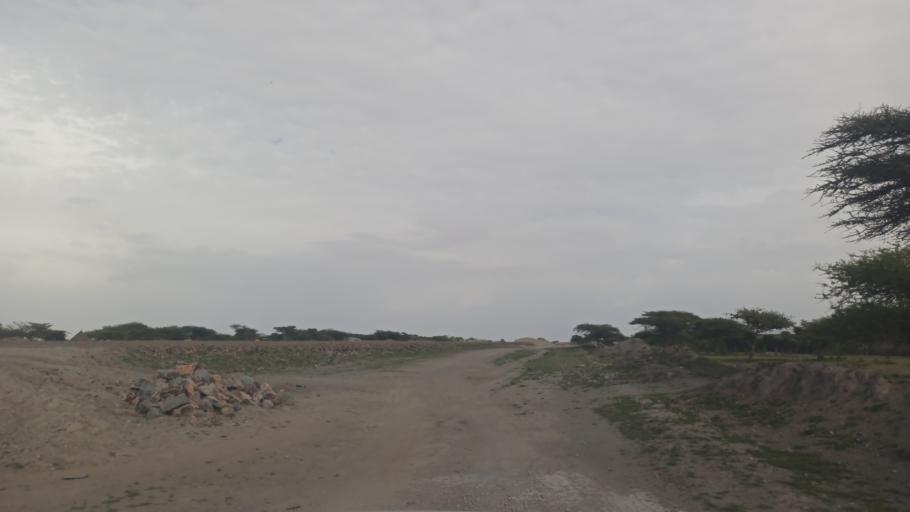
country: ET
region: Oromiya
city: Ziway
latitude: 7.6788
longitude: 38.6745
